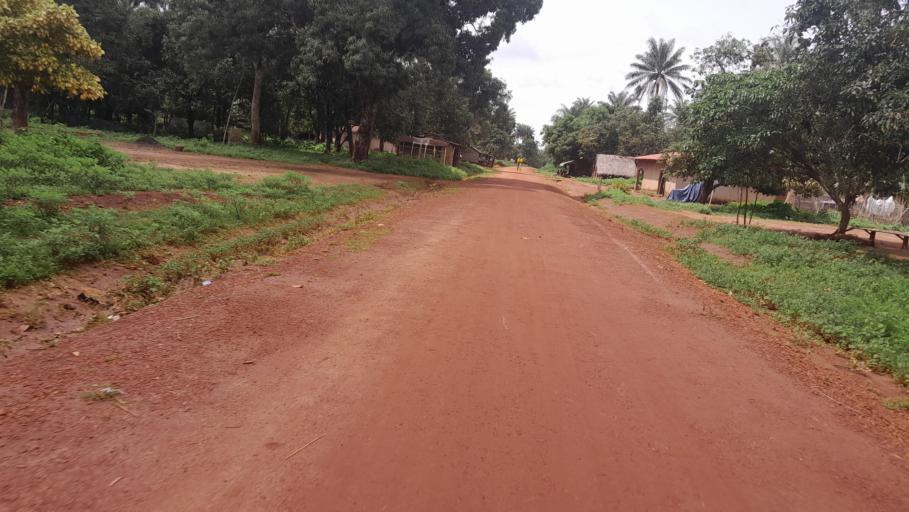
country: GN
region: Boke
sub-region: Boffa
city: Boffa
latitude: 10.0089
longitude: -13.8867
